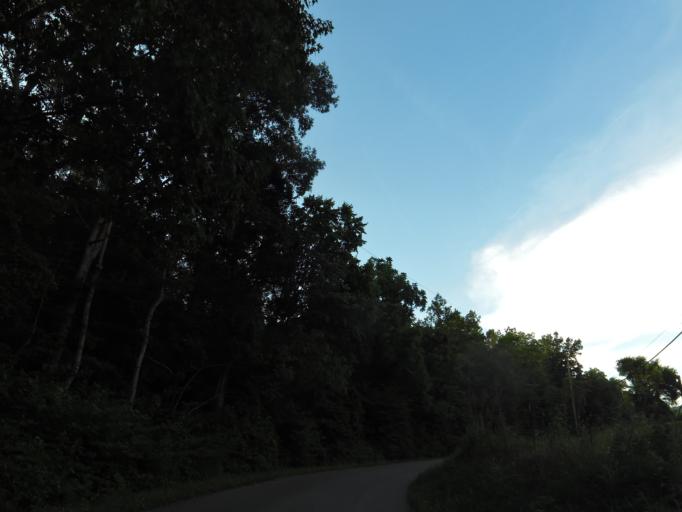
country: US
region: Tennessee
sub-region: Blount County
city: Eagleton Village
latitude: 35.8266
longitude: -83.9186
